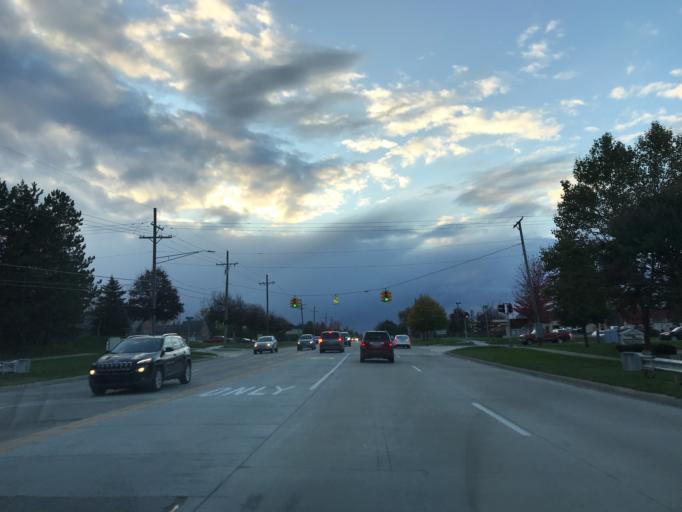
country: US
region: Michigan
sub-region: Oakland County
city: Farmington
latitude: 42.4404
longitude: -83.3843
